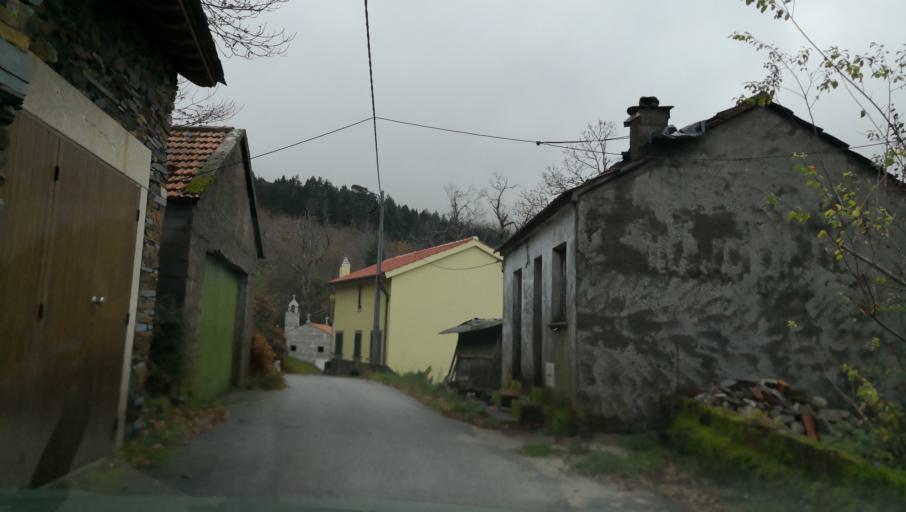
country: PT
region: Vila Real
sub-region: Mondim de Basto
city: Mondim de Basto
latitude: 41.3168
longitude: -7.8758
